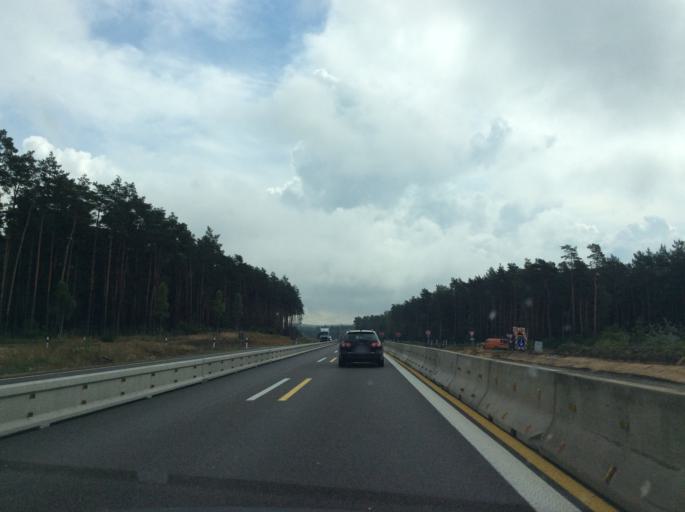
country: DE
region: Brandenburg
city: Storkow
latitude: 52.3116
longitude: 13.9540
